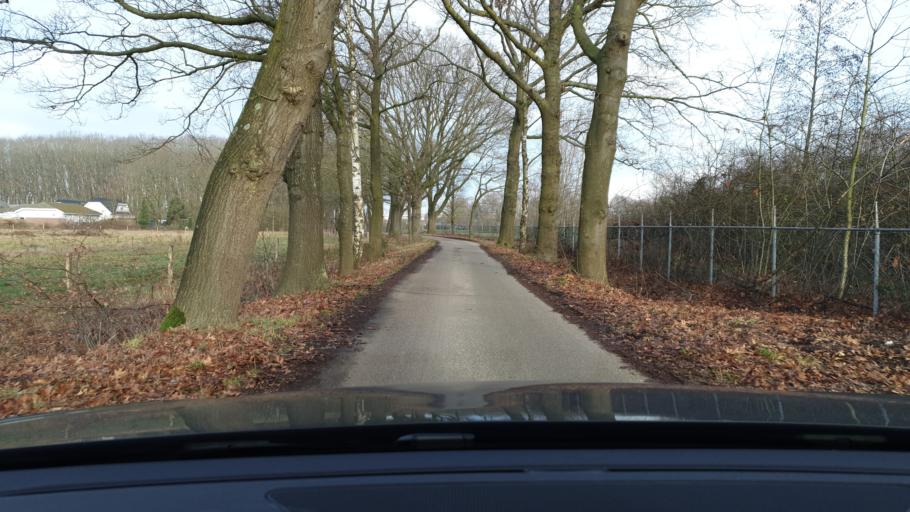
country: NL
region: North Brabant
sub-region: Gemeente Eindhoven
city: Muschberg en Geestenberg
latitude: 51.4229
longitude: 5.5301
